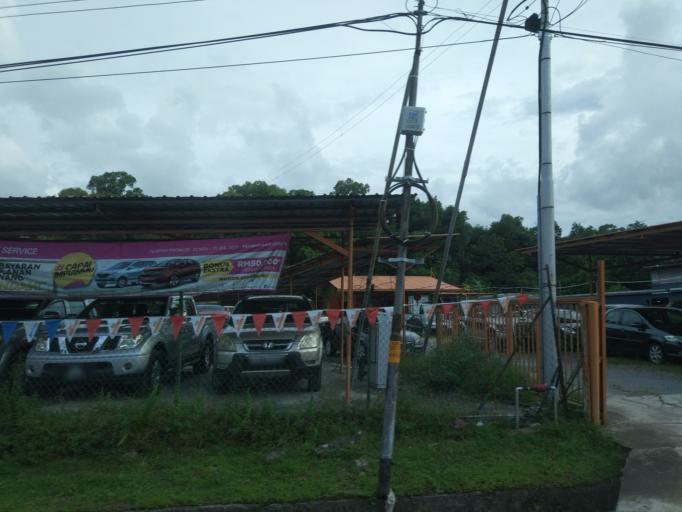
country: MY
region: Sabah
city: Kota Kinabalu
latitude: 5.9929
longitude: 116.1153
